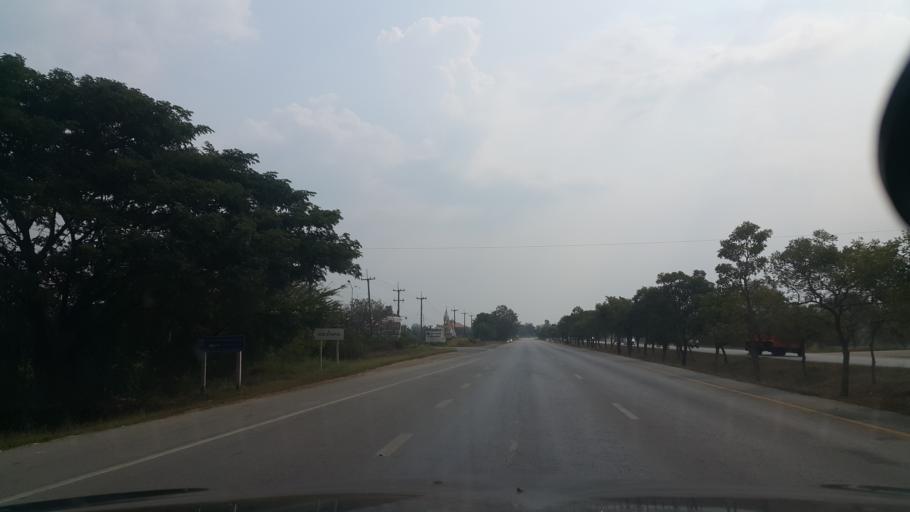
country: TH
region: Sukhothai
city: Sukhothai
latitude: 17.0604
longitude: 99.8918
